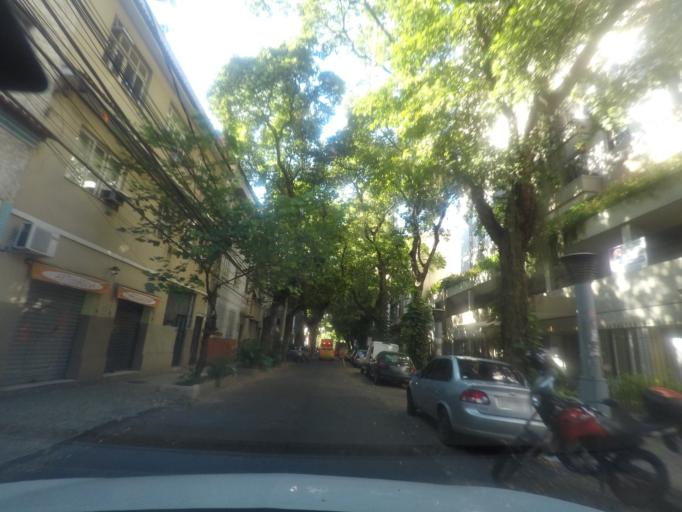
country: BR
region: Rio de Janeiro
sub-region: Rio De Janeiro
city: Rio de Janeiro
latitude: -22.9512
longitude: -43.1872
